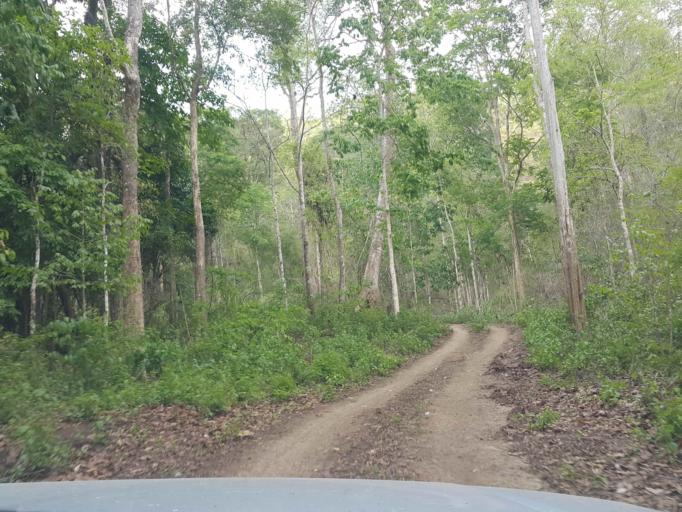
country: TH
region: Chiang Mai
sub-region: Amphoe Chiang Dao
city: Chiang Dao
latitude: 19.3169
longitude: 98.7272
